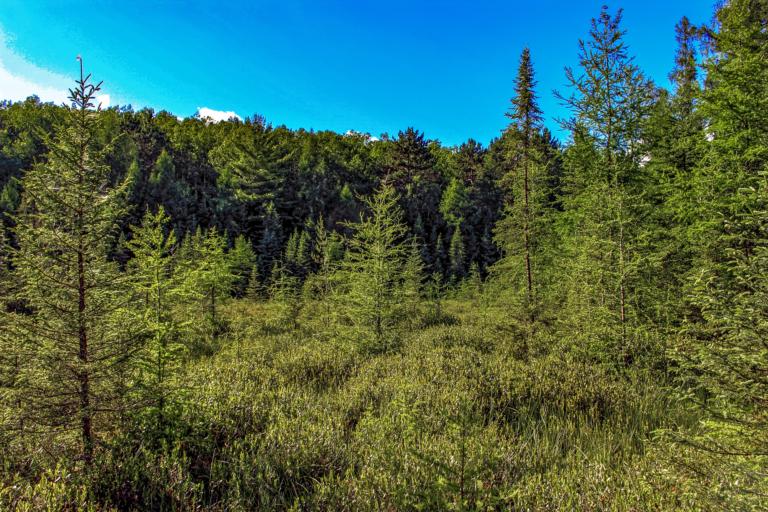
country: US
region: Wisconsin
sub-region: Vilas County
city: Eagle River
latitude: 46.0233
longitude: -89.5560
